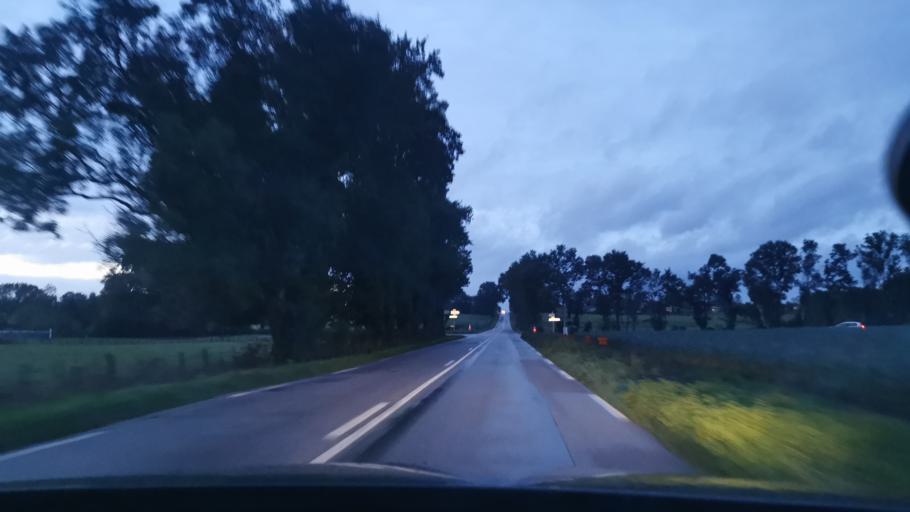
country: FR
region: Rhone-Alpes
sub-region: Departement de l'Ain
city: Bage-la-Ville
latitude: 46.3453
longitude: 4.9398
